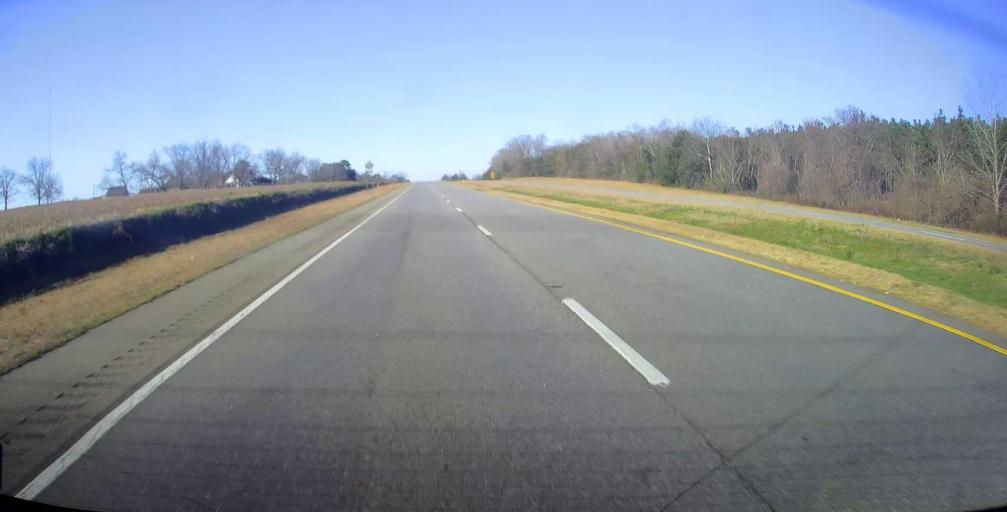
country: US
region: Georgia
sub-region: Sumter County
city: Americus
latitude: 31.9427
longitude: -84.2557
